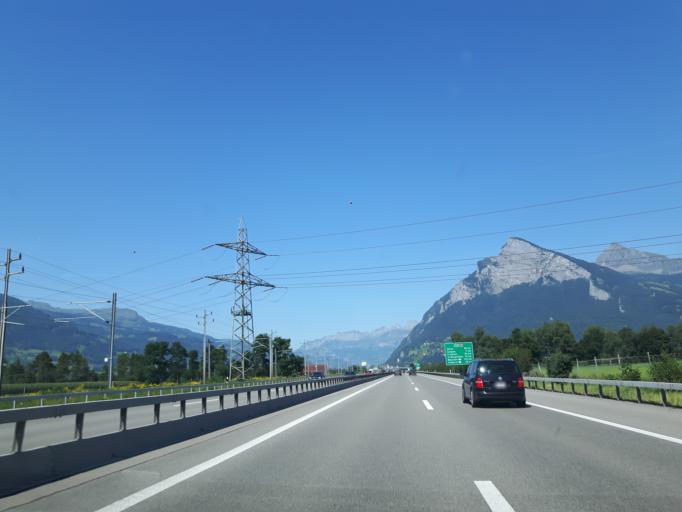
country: CH
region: Saint Gallen
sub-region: Wahlkreis Sarganserland
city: Bad Ragaz
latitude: 47.0226
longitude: 9.4835
